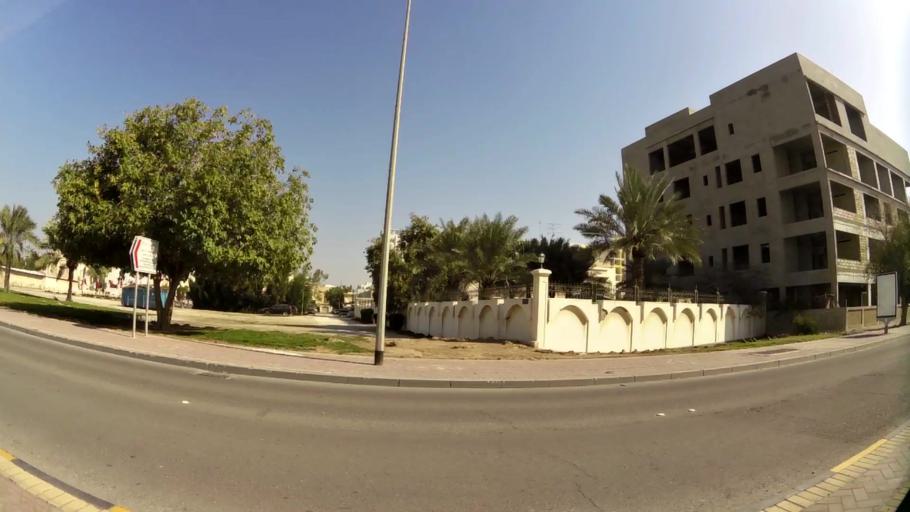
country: BH
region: Manama
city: Manama
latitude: 26.2124
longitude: 50.5844
